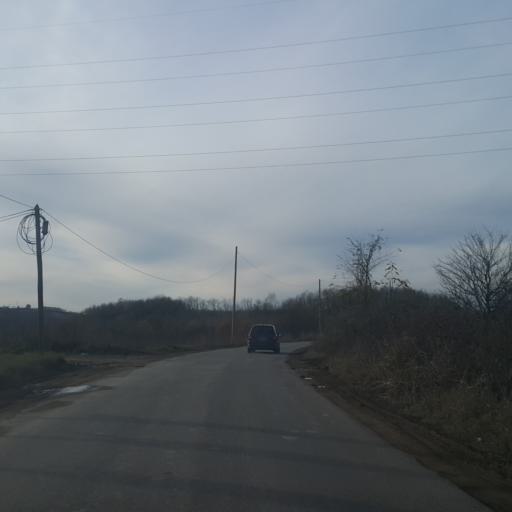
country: RS
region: Central Serbia
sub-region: Belgrade
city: Lazarevac
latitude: 44.4018
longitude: 20.3556
